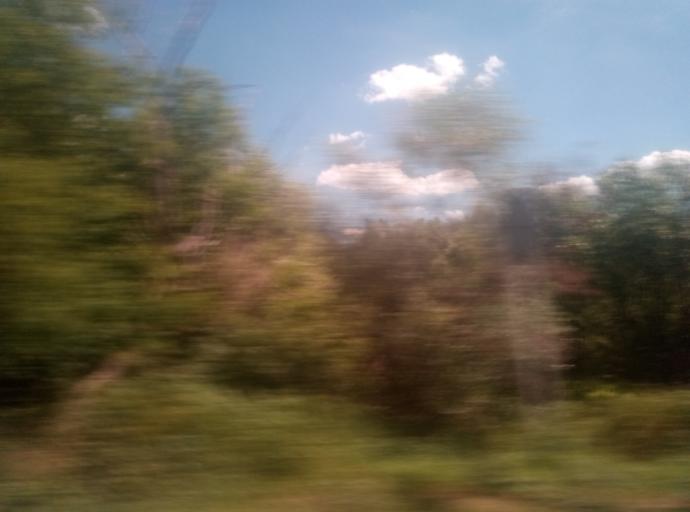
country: RU
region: Tula
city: Kireyevsk
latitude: 53.9722
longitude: 37.9301
